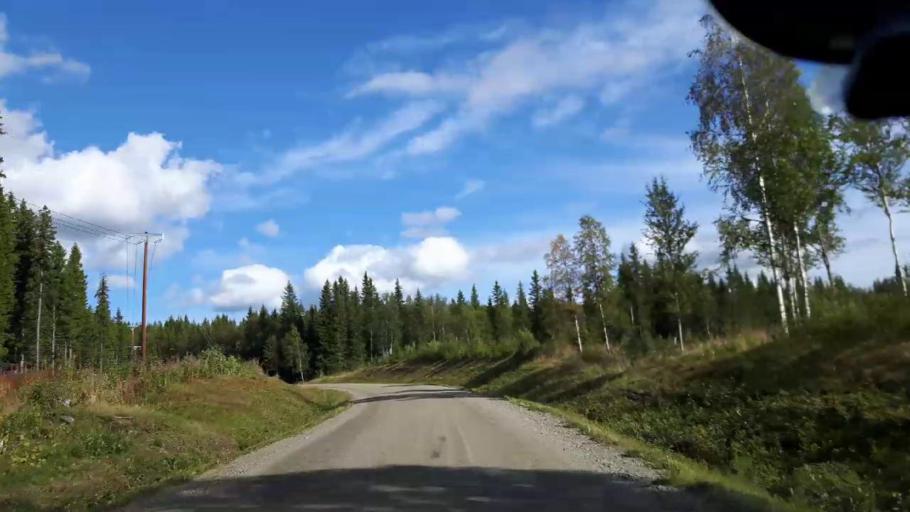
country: SE
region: Jaemtland
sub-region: Ragunda Kommun
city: Hammarstrand
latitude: 63.4419
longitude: 15.9625
